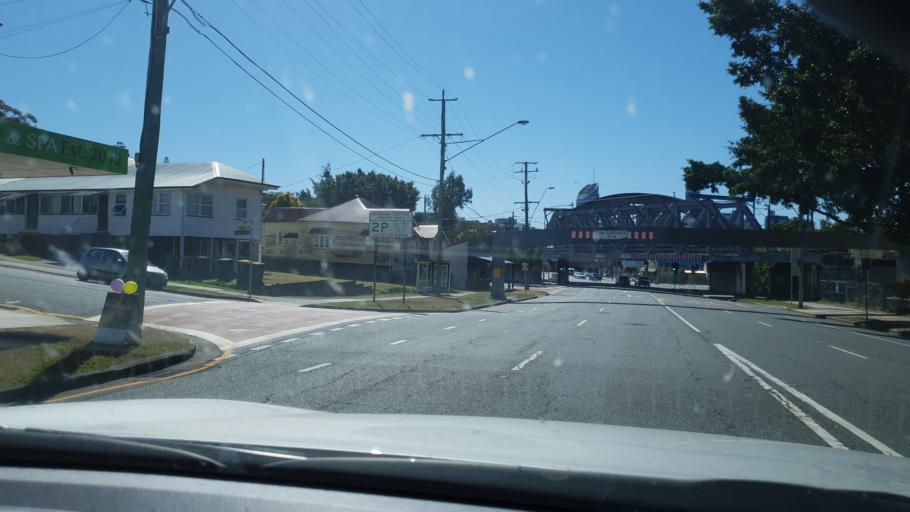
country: AU
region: Queensland
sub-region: Brisbane
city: Woolloongabba
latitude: -27.4929
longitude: 153.0275
